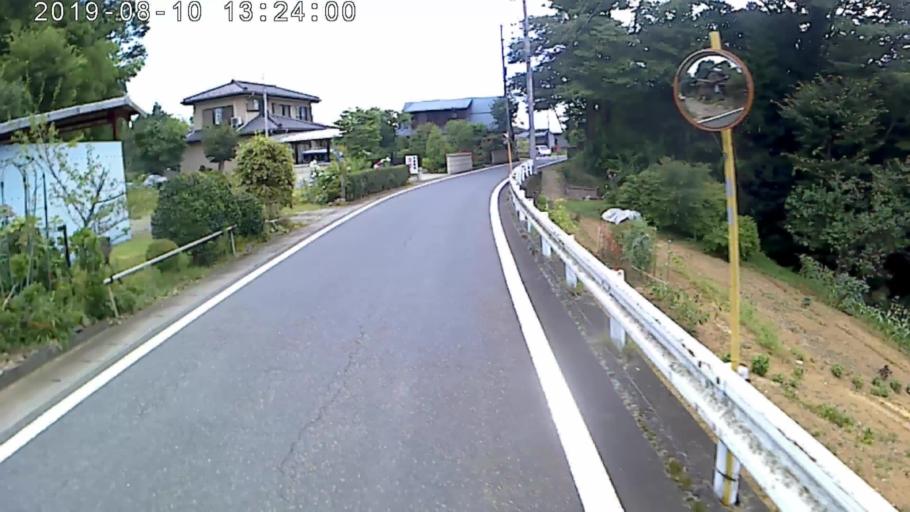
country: JP
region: Yamanashi
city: Uenohara
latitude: 35.6310
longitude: 139.0859
